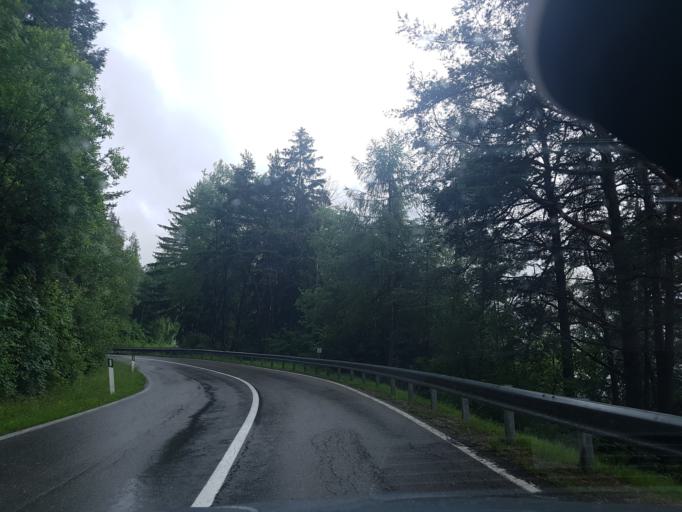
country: IT
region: Trentino-Alto Adige
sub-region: Bolzano
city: Laion
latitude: 46.6003
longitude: 11.6061
